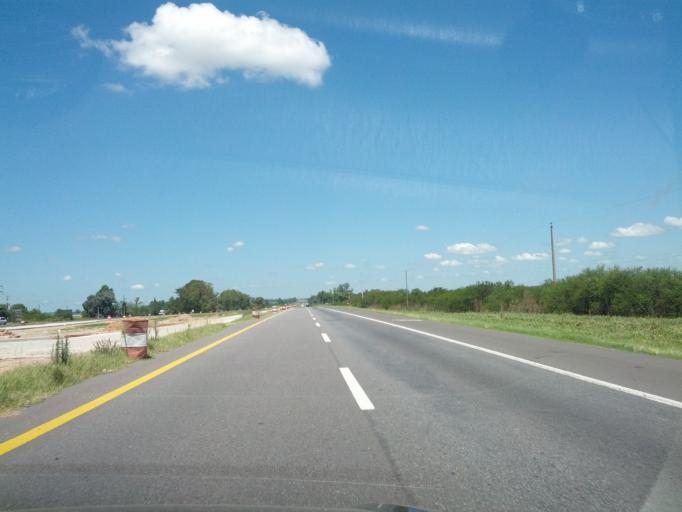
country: AR
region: Entre Rios
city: Gualeguaychu
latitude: -33.1170
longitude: -58.6510
